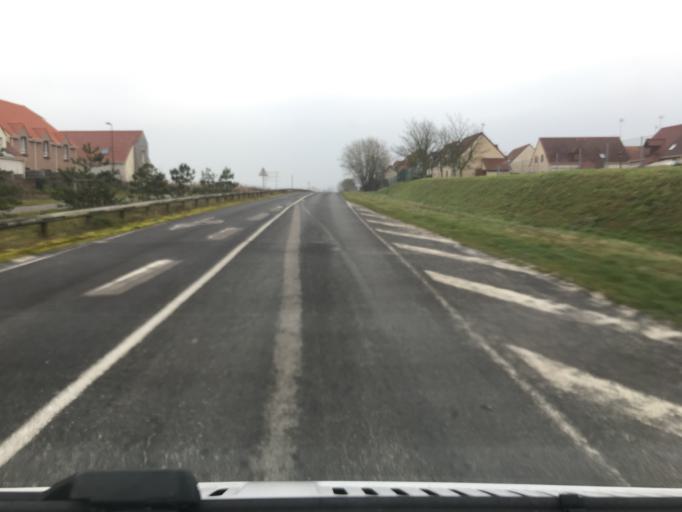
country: FR
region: Picardie
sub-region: Departement de la Somme
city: Le Crotoy
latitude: 50.2283
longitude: 1.6149
